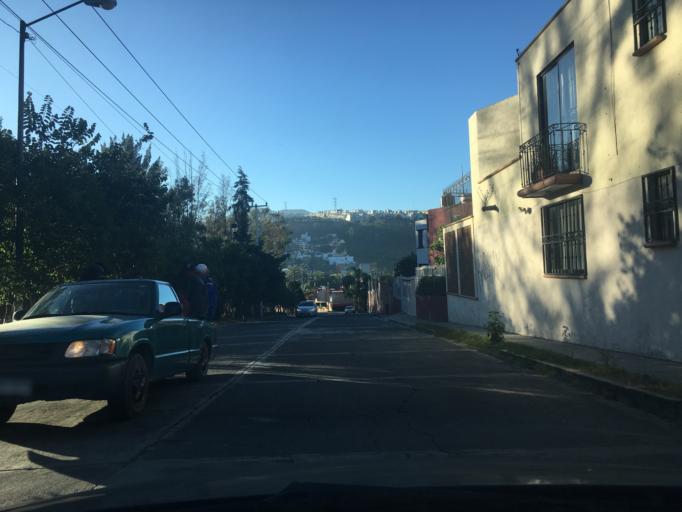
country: MX
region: Michoacan
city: Morelia
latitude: 19.6711
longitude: -101.2072
